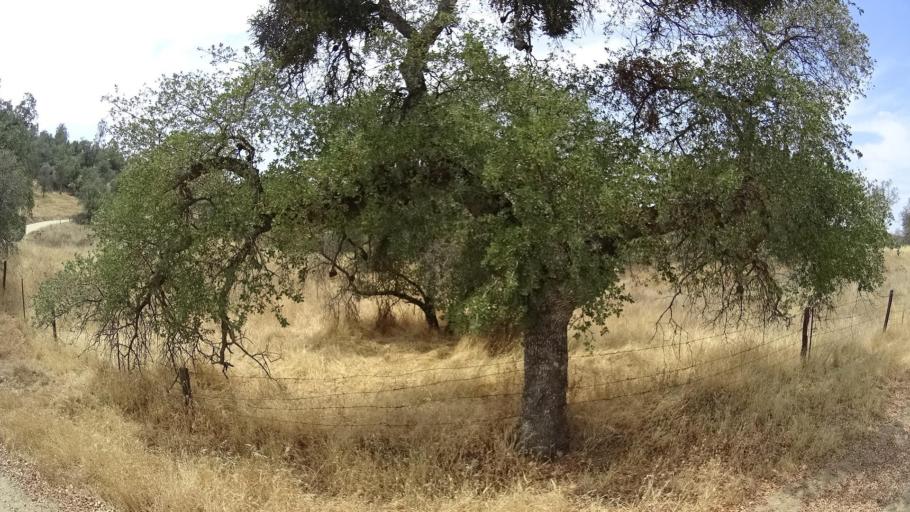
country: US
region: California
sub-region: Madera County
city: Ahwahnee
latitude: 37.3479
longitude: -119.8701
